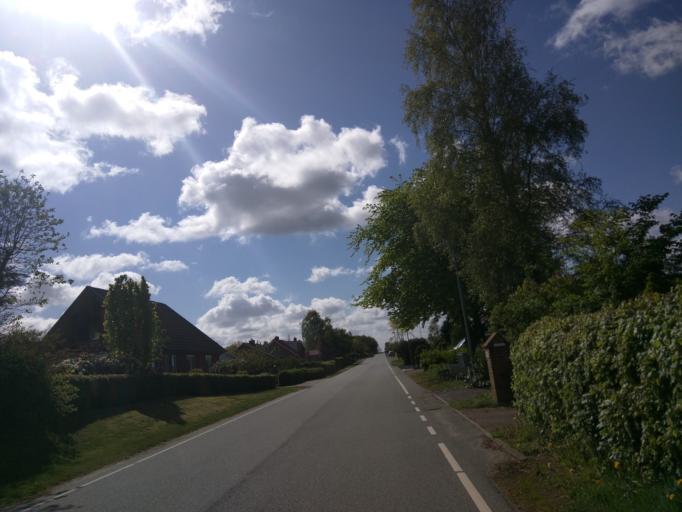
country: DK
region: Central Jutland
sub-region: Viborg Kommune
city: Viborg
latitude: 56.3977
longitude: 9.4370
